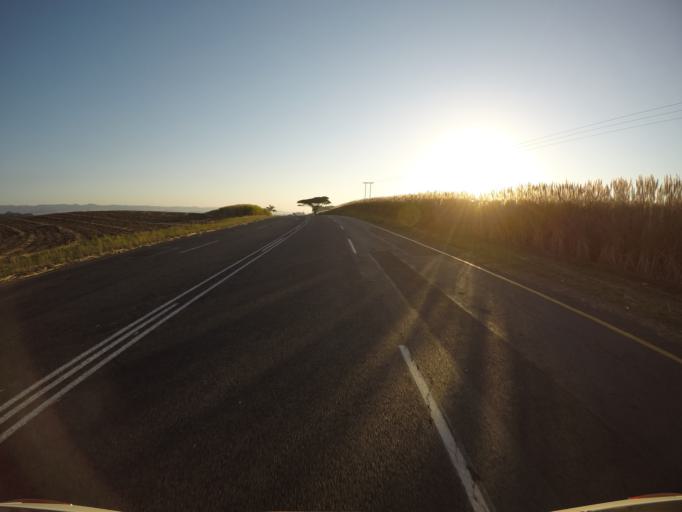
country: ZA
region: KwaZulu-Natal
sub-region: uThungulu District Municipality
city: eSikhawini
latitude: -28.9406
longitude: 31.7397
